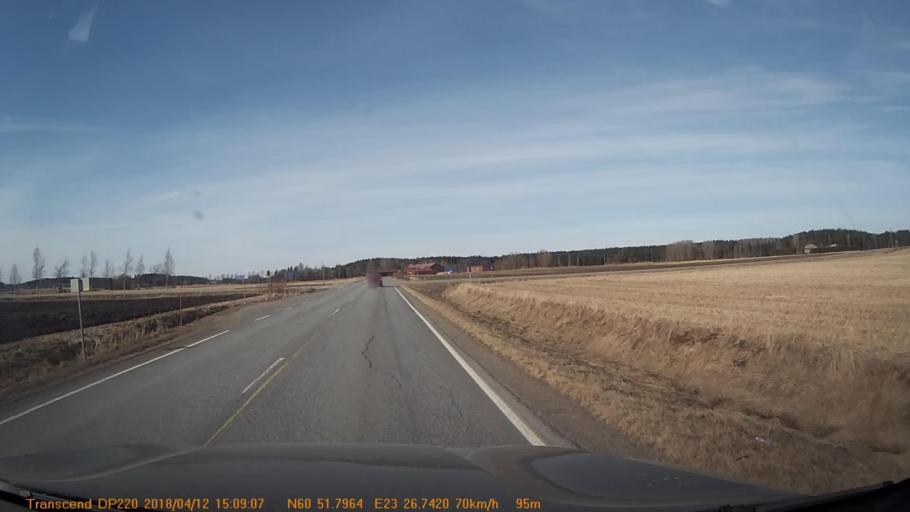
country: FI
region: Haeme
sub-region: Forssa
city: Jokioinen
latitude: 60.8631
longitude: 23.4458
